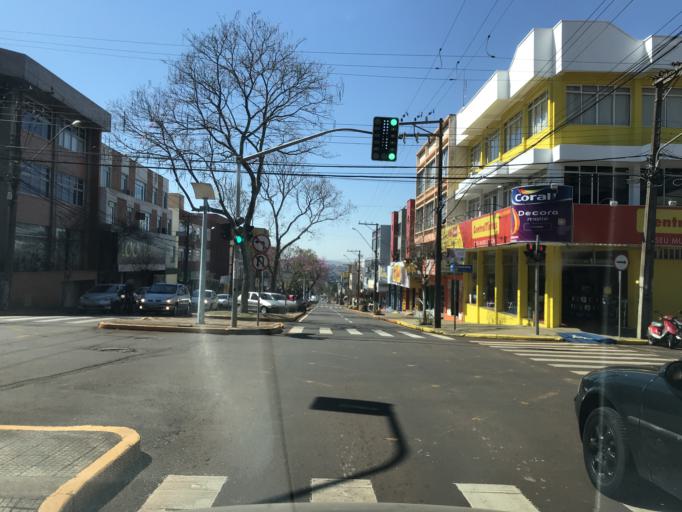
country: BR
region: Parana
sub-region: Toledo
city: Toledo
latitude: -24.7343
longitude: -53.7410
